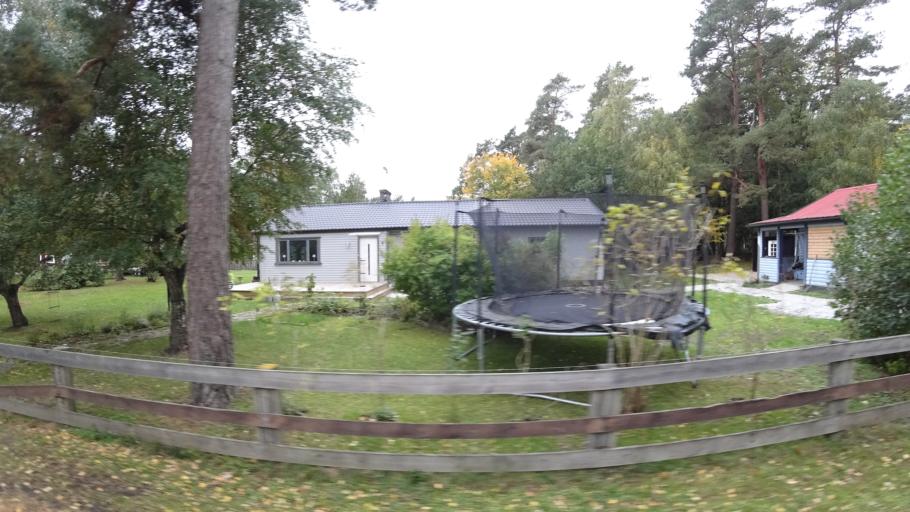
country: SE
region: Skane
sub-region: Kavlinge Kommun
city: Hofterup
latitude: 55.8129
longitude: 12.9730
